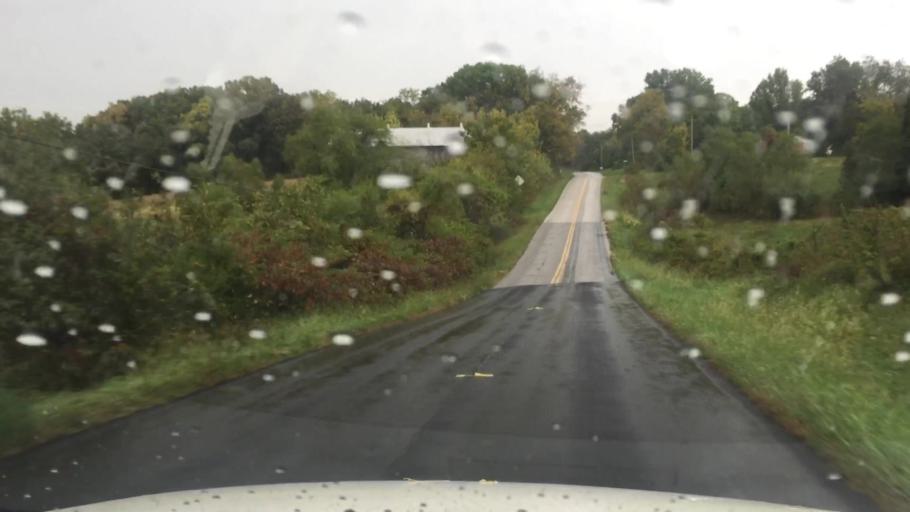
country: US
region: Missouri
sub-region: Boone County
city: Columbia
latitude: 38.9437
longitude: -92.4965
